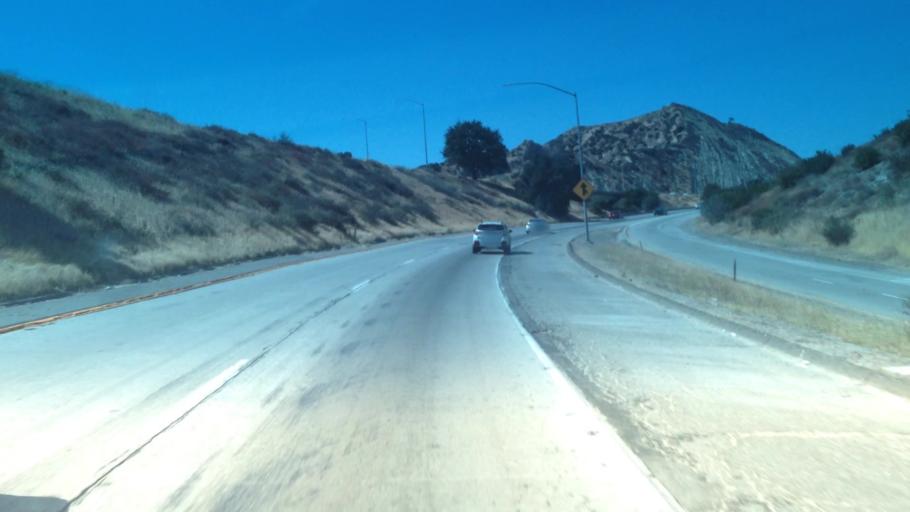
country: US
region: California
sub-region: Los Angeles County
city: Santa Clarita
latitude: 34.3367
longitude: -118.5065
